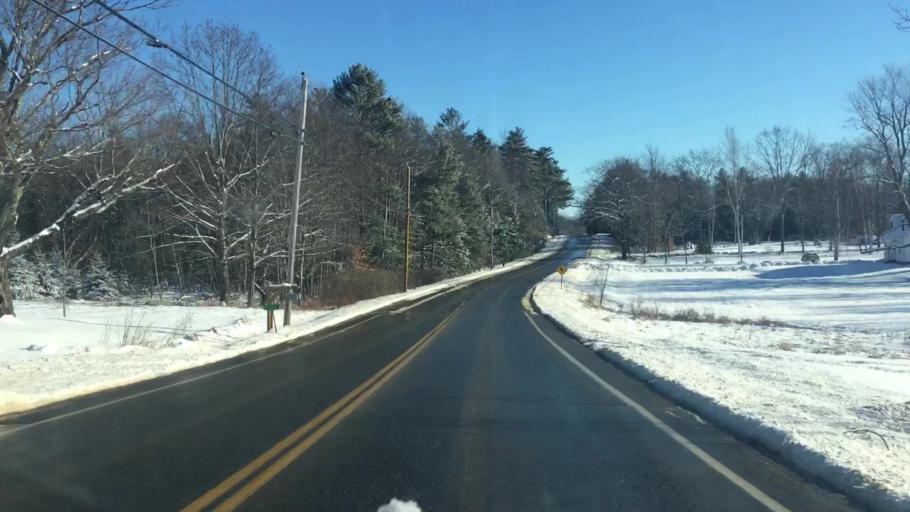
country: US
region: Maine
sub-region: Androscoggin County
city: Lisbon Falls
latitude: 43.9331
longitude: -70.0558
